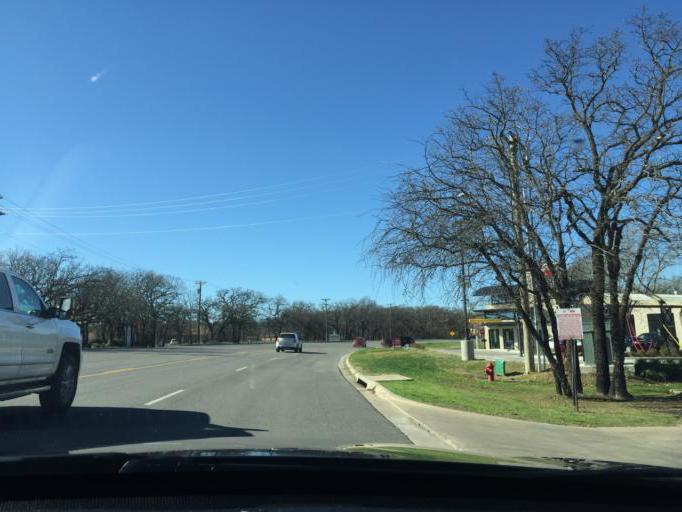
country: US
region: Texas
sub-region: Parker County
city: Weatherford
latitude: 32.7399
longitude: -97.7792
